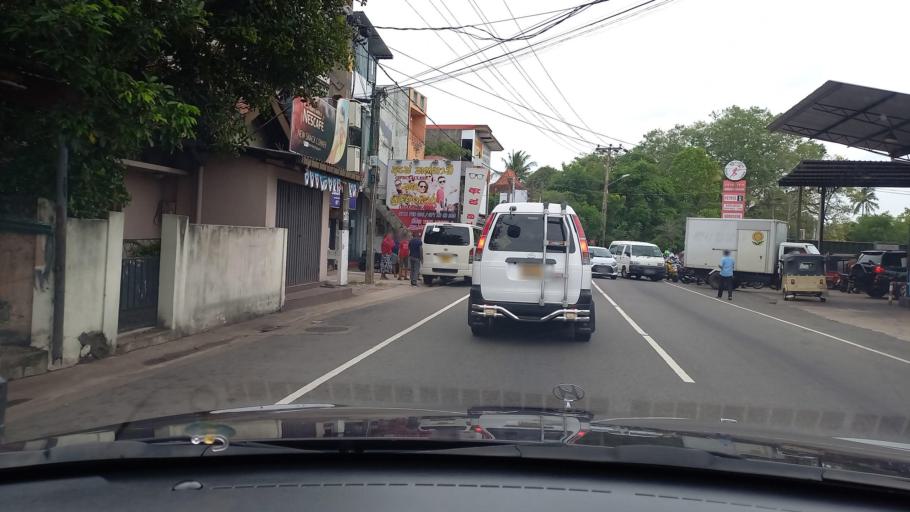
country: LK
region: Western
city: Sri Jayewardenepura Kotte
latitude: 6.8803
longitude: 79.8997
